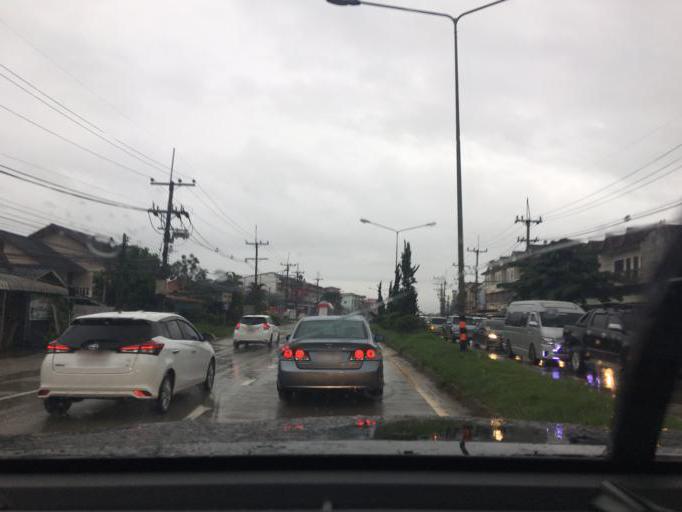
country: TH
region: Chiang Rai
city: Mae Chan
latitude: 20.0453
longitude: 99.8763
